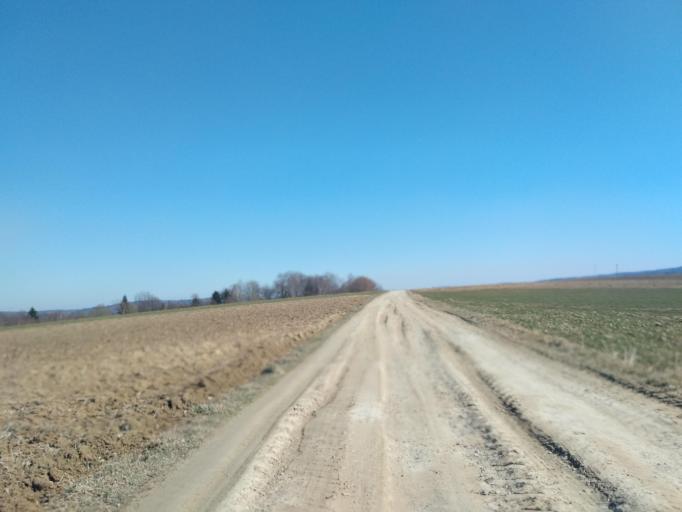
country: PL
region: Subcarpathian Voivodeship
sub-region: Powiat ropczycko-sedziszowski
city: Wielopole Skrzynskie
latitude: 49.9506
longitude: 21.5718
